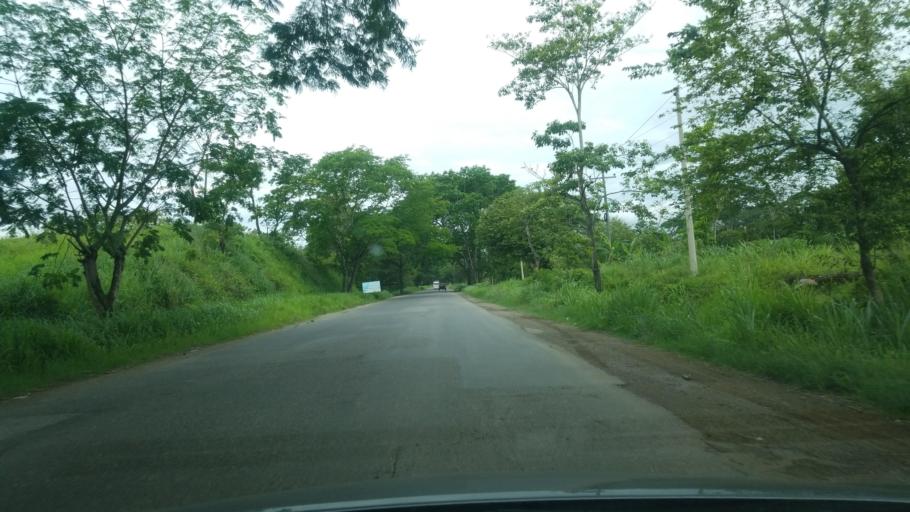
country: HN
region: Santa Barbara
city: La Flecha
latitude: 15.2967
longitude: -88.4650
